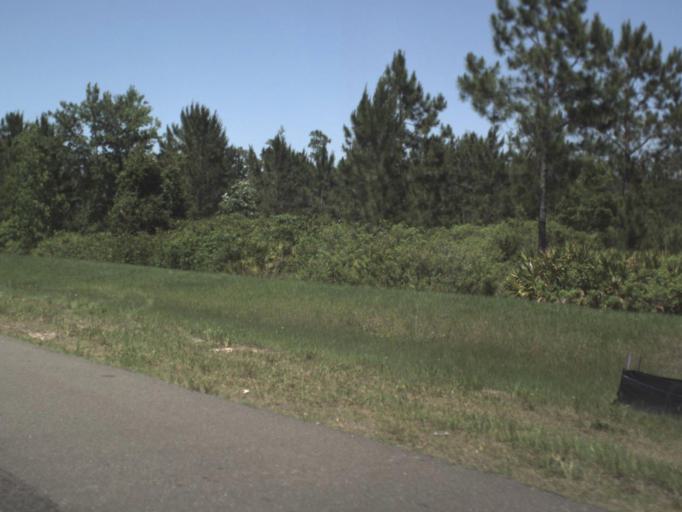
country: US
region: Florida
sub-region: Duval County
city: Baldwin
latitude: 30.2884
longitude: -81.8786
